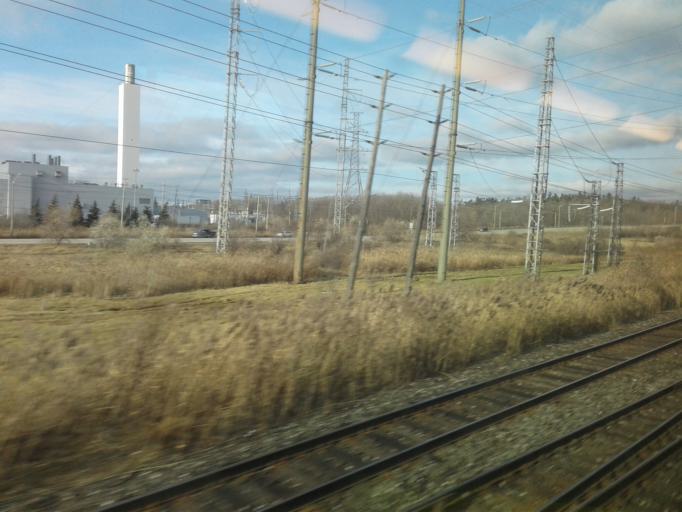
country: CA
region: Ontario
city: Oakville
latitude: 43.4831
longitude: -79.6594
